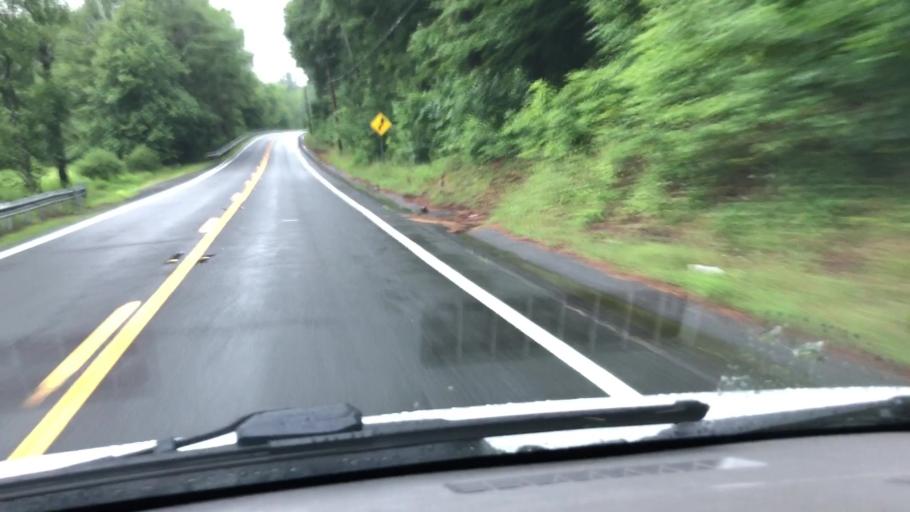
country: US
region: Massachusetts
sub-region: Hampshire County
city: Chesterfield
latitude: 42.3621
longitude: -72.9076
